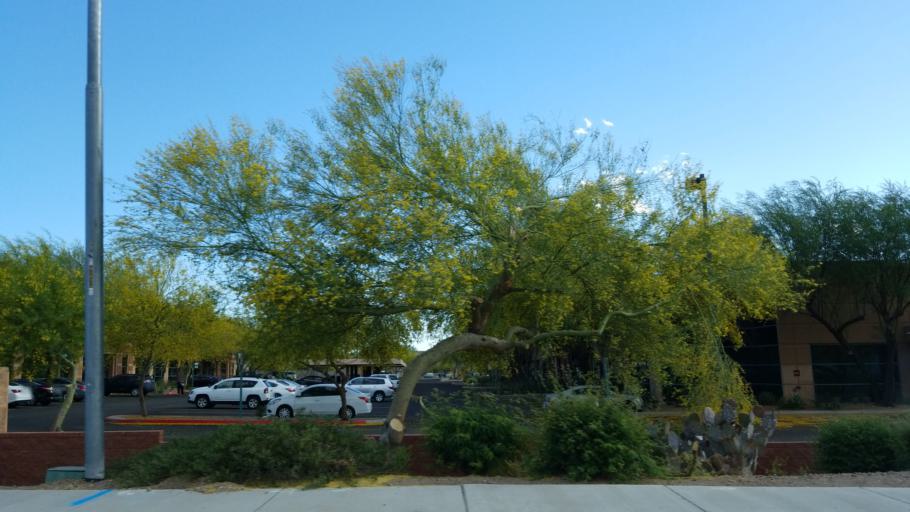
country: US
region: Arizona
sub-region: Maricopa County
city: Anthem
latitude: 33.6984
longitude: -112.1022
